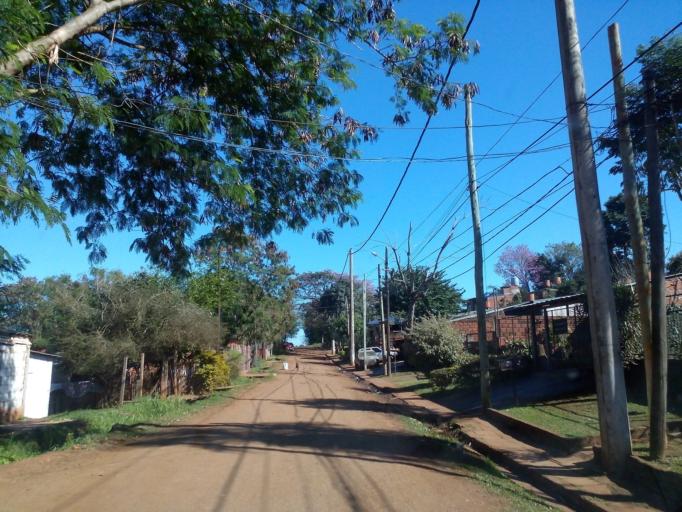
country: AR
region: Misiones
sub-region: Departamento de Capital
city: Posadas
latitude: -27.3864
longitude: -55.9430
